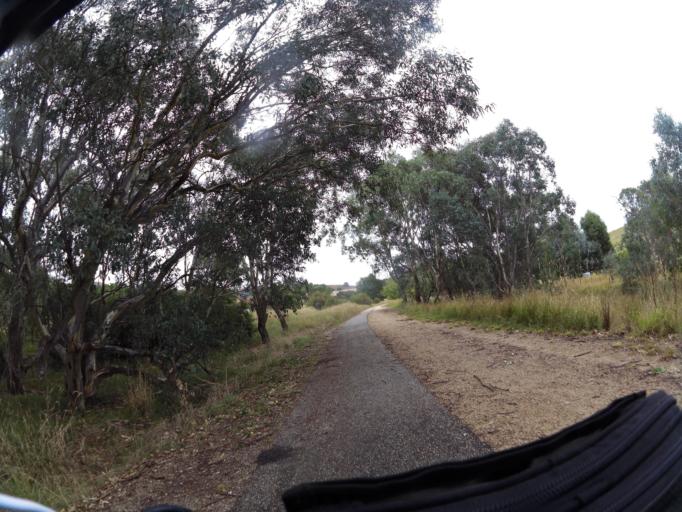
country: AU
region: New South Wales
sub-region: Albury Municipality
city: East Albury
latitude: -36.2260
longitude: 147.1250
